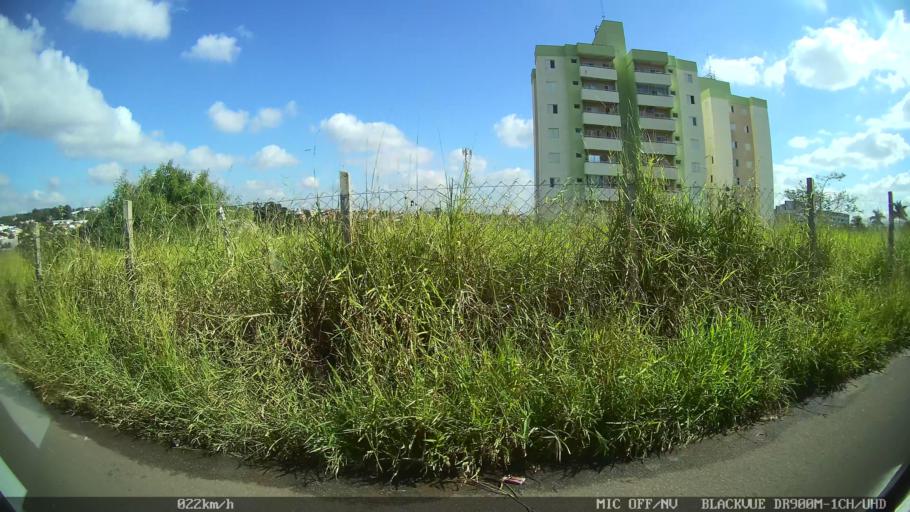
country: BR
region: Sao Paulo
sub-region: Hortolandia
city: Hortolandia
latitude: -22.8717
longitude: -47.2174
